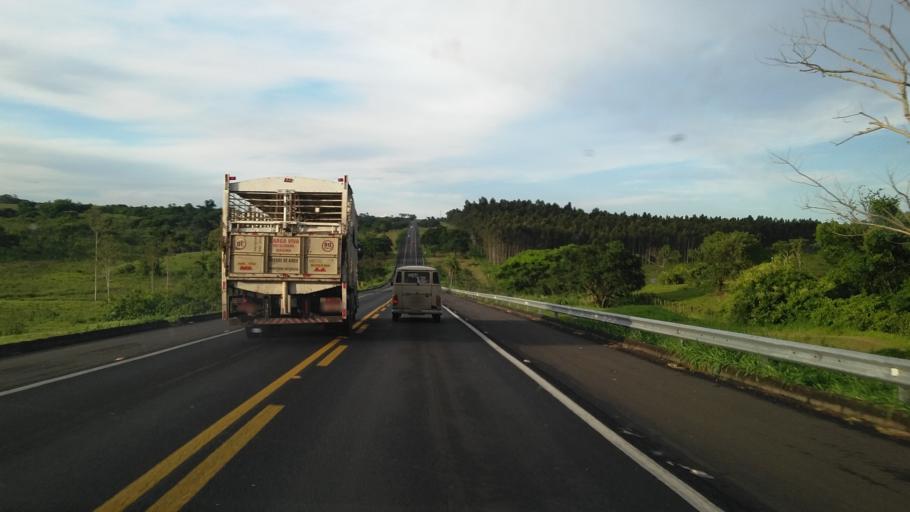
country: BR
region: Sao Paulo
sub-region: Marilia
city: Marilia
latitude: -21.9357
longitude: -49.9194
